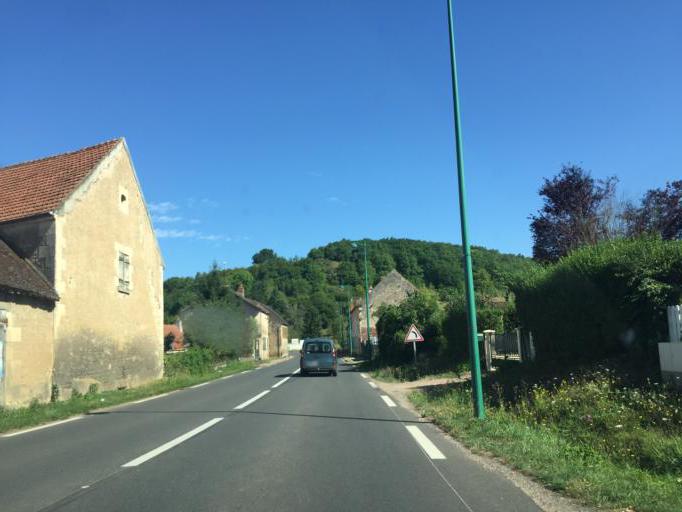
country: FR
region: Bourgogne
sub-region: Departement de la Nievre
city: Clamecy
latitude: 47.4562
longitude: 3.5504
